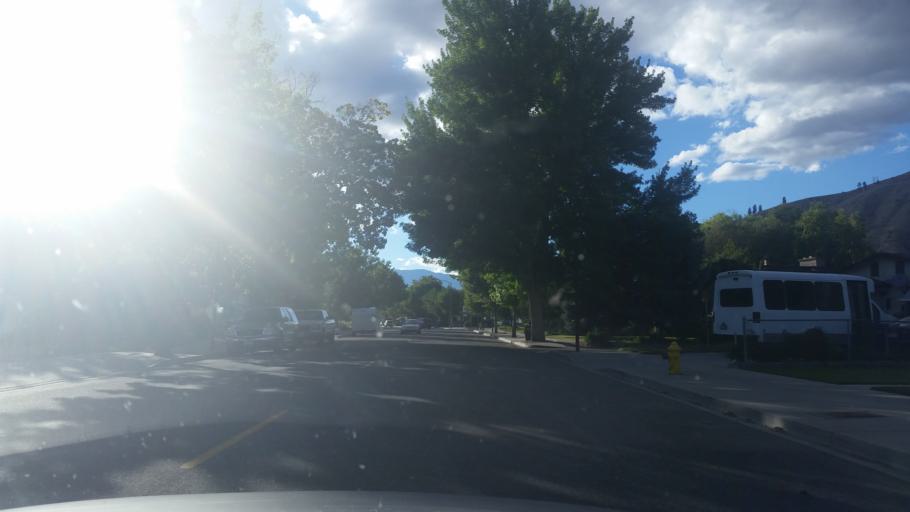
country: US
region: Washington
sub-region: Chelan County
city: Cashmere
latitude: 47.5212
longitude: -120.4639
